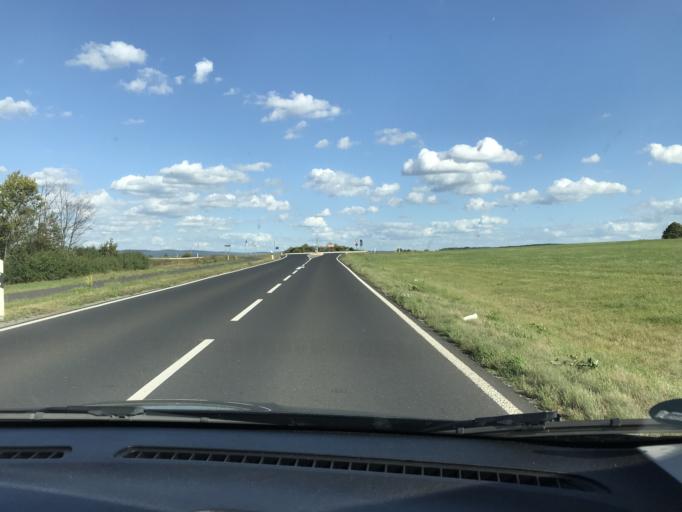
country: DE
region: Hesse
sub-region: Regierungsbezirk Darmstadt
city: Schaafheim
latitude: 49.9245
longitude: 9.0406
